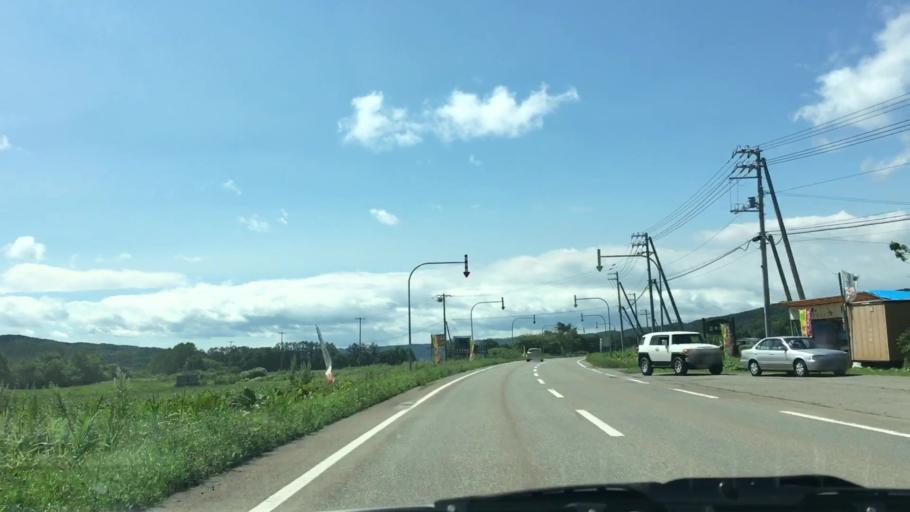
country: JP
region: Hokkaido
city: Otofuke
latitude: 43.2801
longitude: 143.6235
